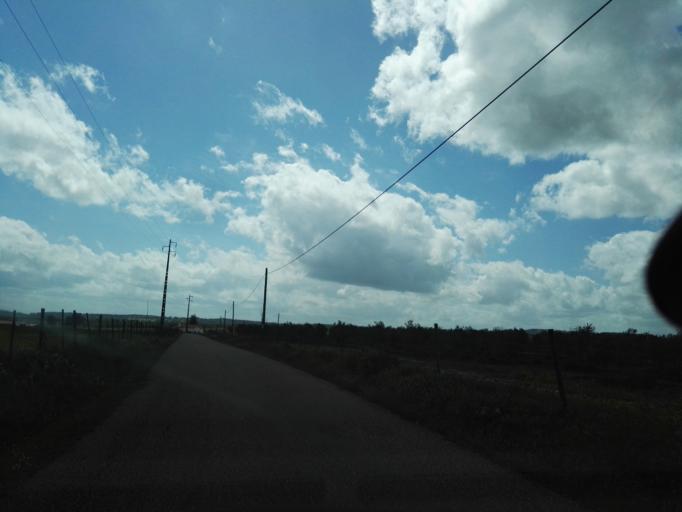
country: PT
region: Portalegre
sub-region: Elvas
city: Elvas
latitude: 38.9499
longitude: -7.1880
